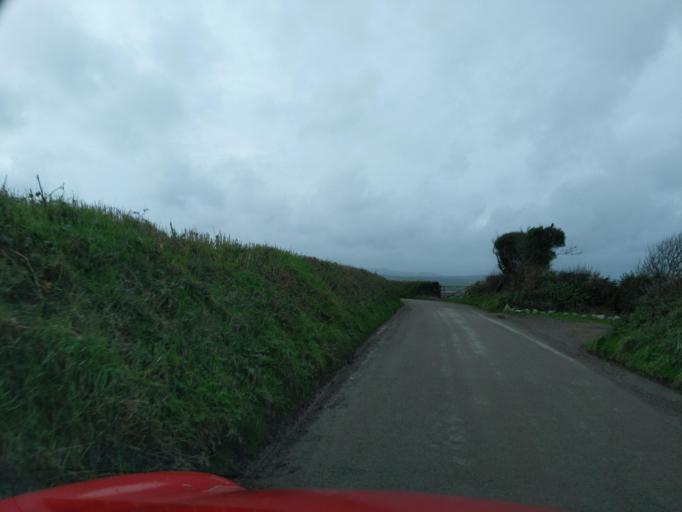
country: GB
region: England
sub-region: Cornwall
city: Fowey
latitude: 50.3443
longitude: -4.5597
